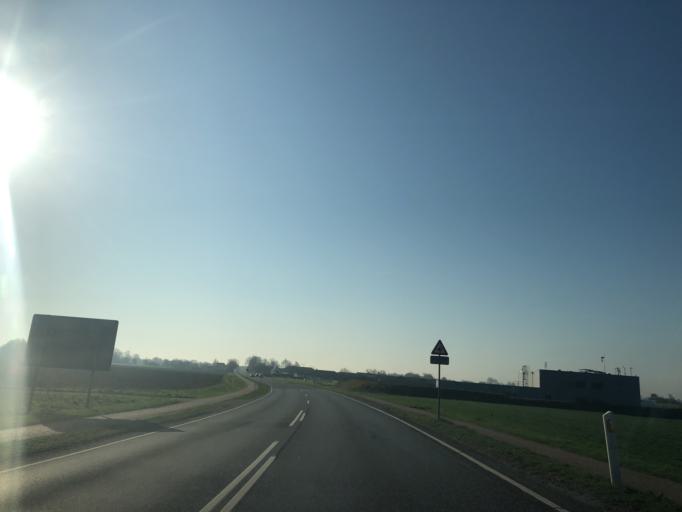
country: DK
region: Zealand
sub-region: Ringsted Kommune
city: Ringsted
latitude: 55.4300
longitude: 11.8089
